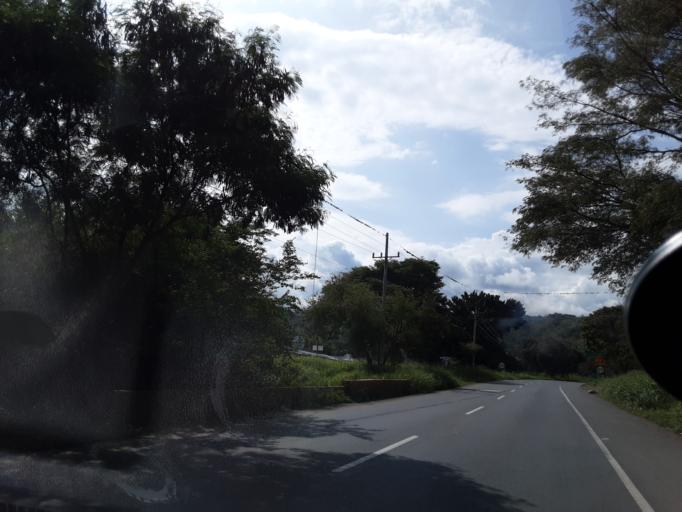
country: CO
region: Valle del Cauca
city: Buga
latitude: 3.8626
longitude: -76.2989
